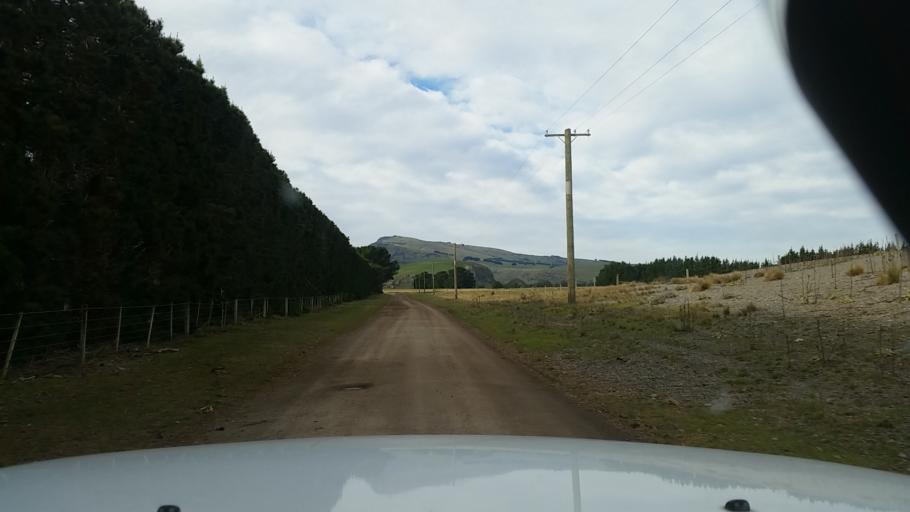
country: NZ
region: Canterbury
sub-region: Selwyn District
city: Lincoln
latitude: -43.8107
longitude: 172.6719
